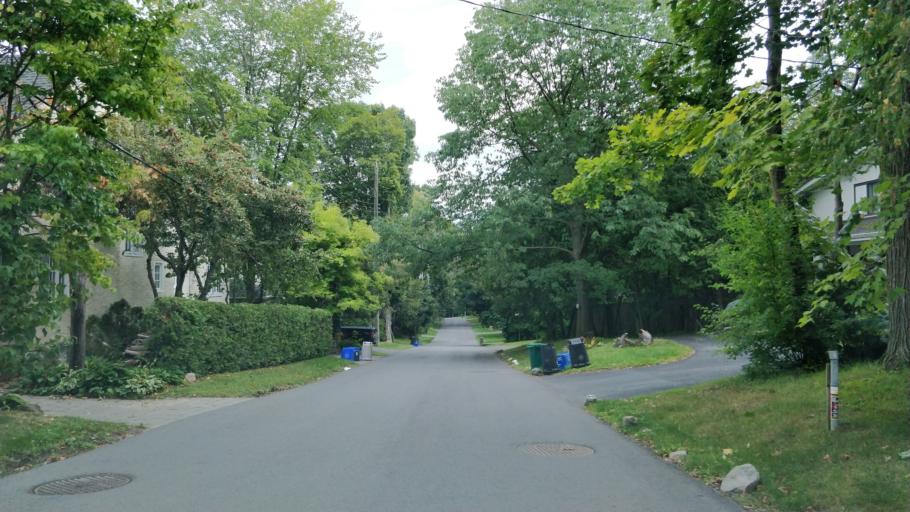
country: CA
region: Quebec
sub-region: Outaouais
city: Gatineau
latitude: 45.4492
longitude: -75.6736
